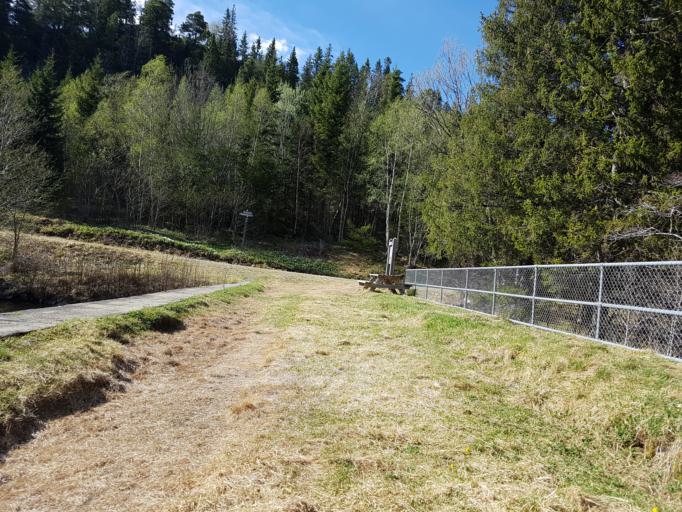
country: NO
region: Sor-Trondelag
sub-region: Trondheim
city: Trondheim
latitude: 63.4469
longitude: 10.3019
